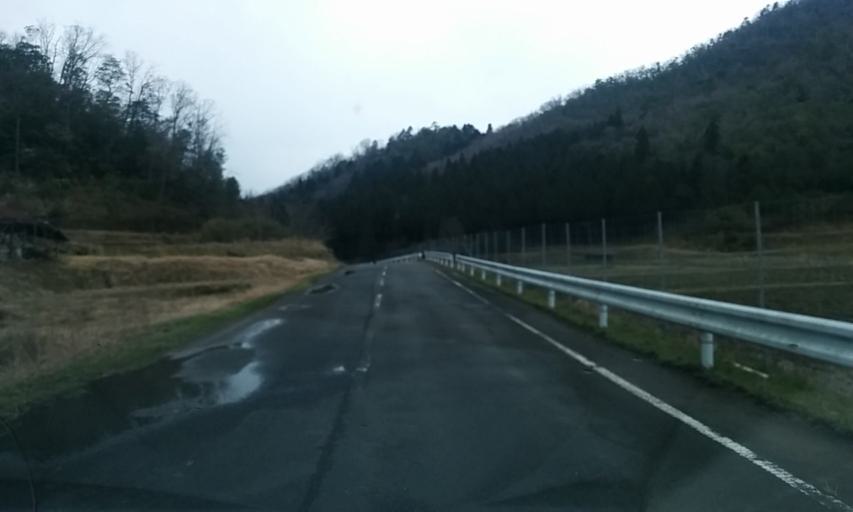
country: JP
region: Kyoto
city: Kameoka
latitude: 35.1182
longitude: 135.4209
